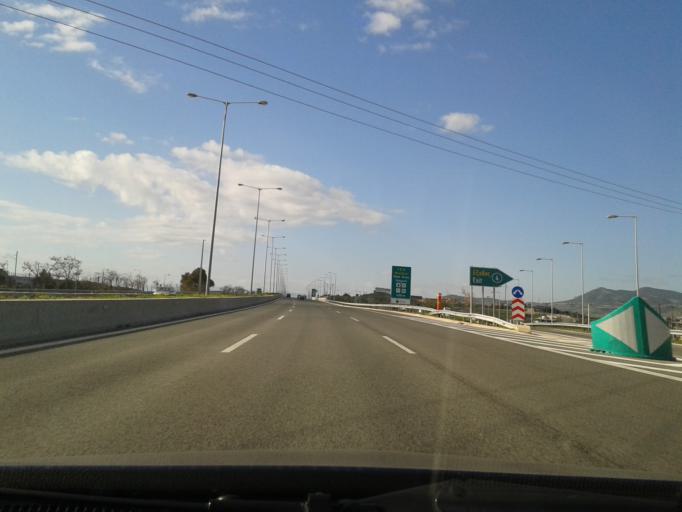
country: GR
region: Attica
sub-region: Nomarchia Dytikis Attikis
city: Megara
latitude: 38.0005
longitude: 23.3746
